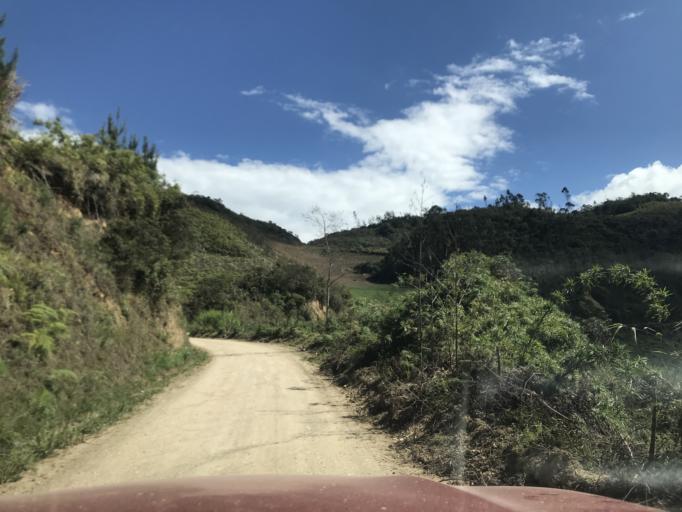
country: PE
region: Cajamarca
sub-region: Provincia de Chota
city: Querocoto
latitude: -6.3484
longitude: -79.0365
